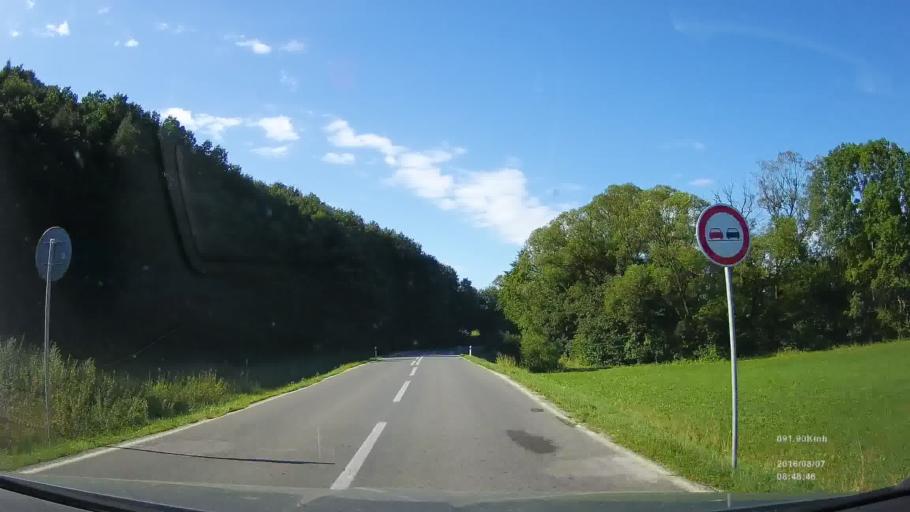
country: SK
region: Presovsky
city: Stropkov
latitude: 49.2582
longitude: 21.6931
